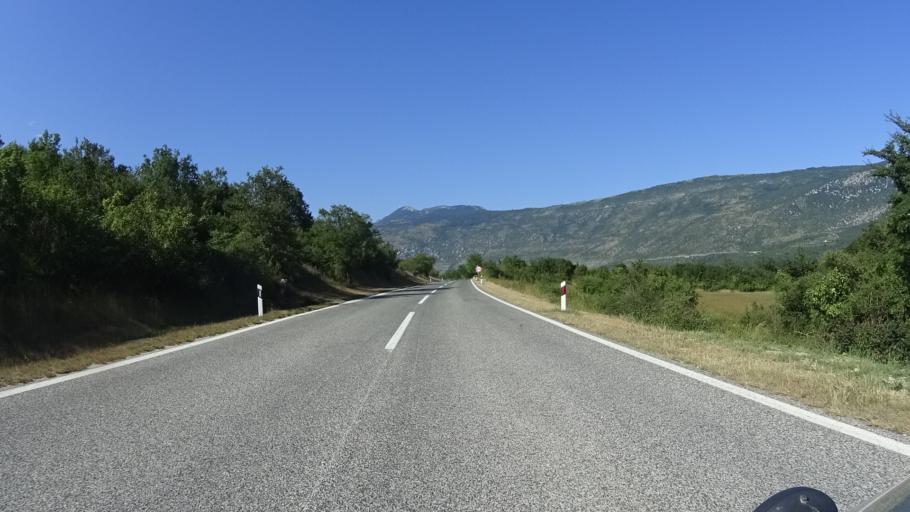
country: HR
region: Istarska
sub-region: Grad Labin
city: Labin
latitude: 45.2104
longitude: 14.1435
